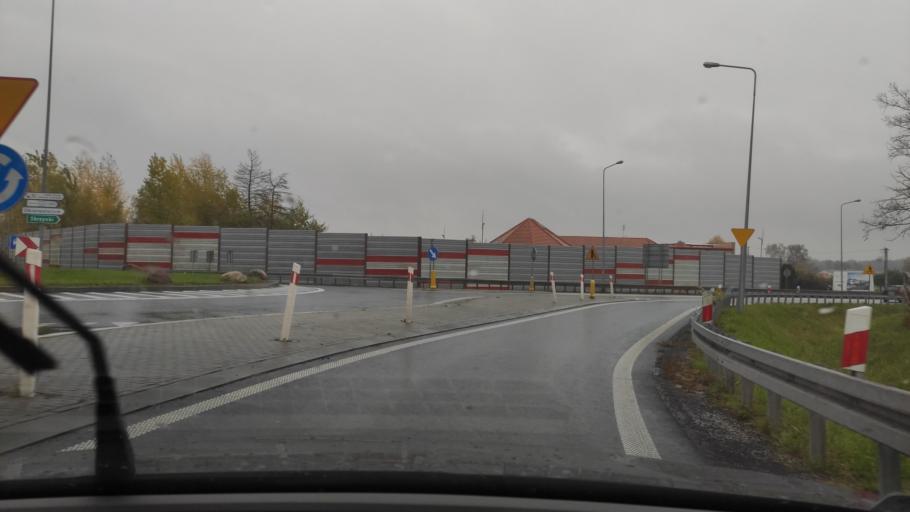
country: PL
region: Greater Poland Voivodeship
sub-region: Powiat poznanski
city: Kornik
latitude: 52.2574
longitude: 17.0790
